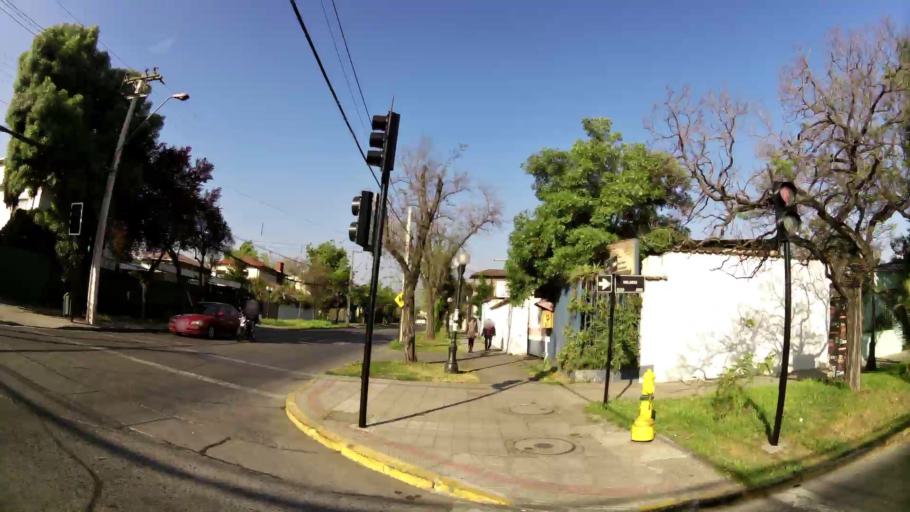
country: CL
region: Santiago Metropolitan
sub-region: Provincia de Santiago
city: Villa Presidente Frei, Nunoa, Santiago, Chile
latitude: -33.4414
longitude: -70.5978
